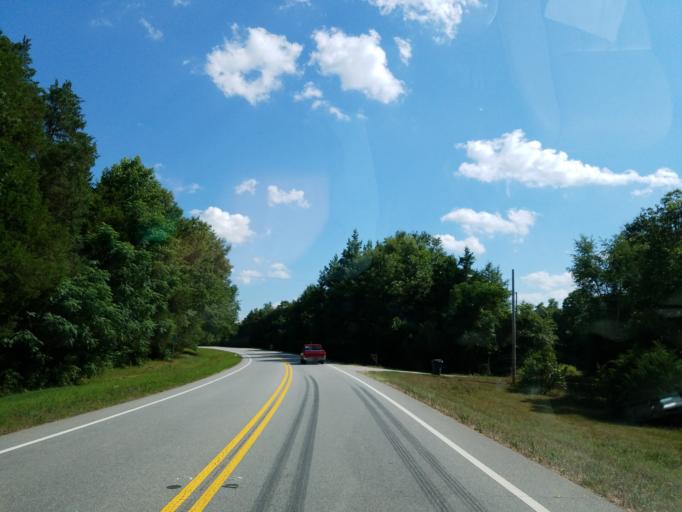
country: US
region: Georgia
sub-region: Lamar County
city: Barnesville
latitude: 32.9935
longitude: -84.1225
